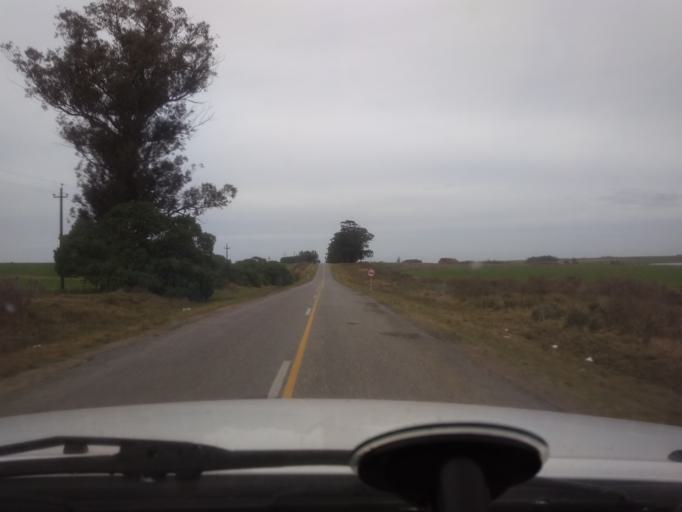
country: UY
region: Canelones
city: San Ramon
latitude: -34.0577
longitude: -55.9015
